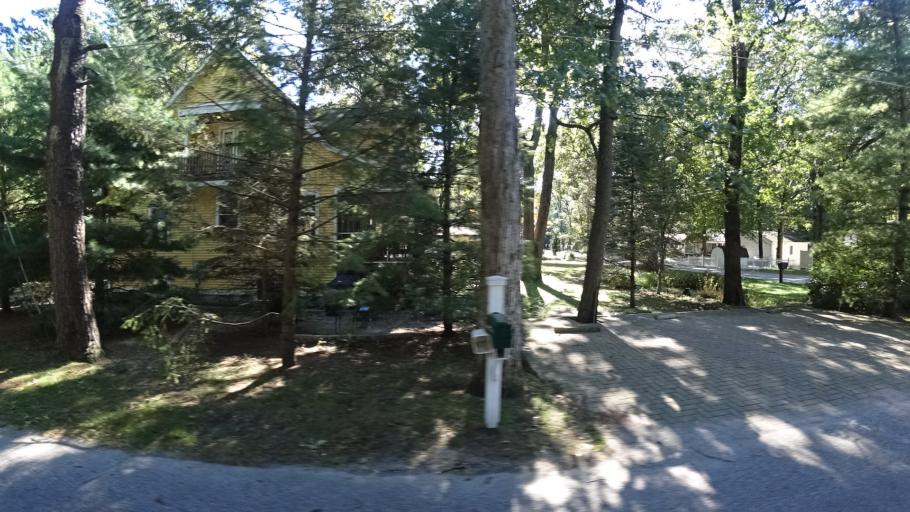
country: US
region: Indiana
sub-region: LaPorte County
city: Long Beach
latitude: 41.7528
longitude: -86.8313
